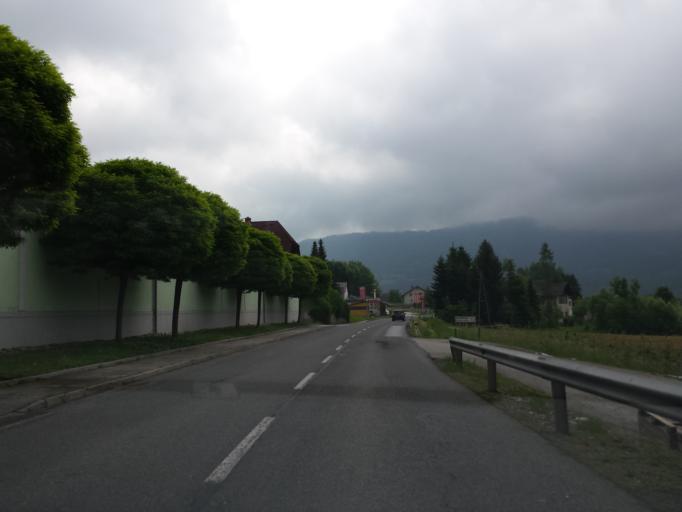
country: AT
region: Styria
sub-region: Politischer Bezirk Weiz
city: Floing
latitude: 47.2508
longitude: 15.7269
